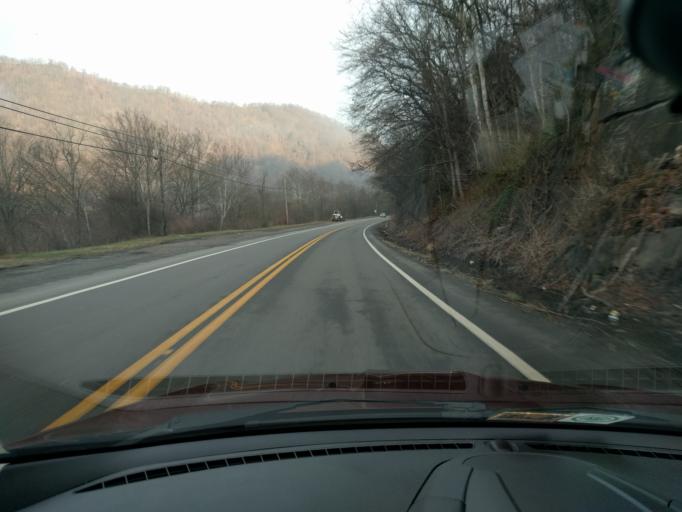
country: US
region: West Virginia
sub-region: Kanawha County
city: Montgomery
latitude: 38.1618
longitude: -81.3002
